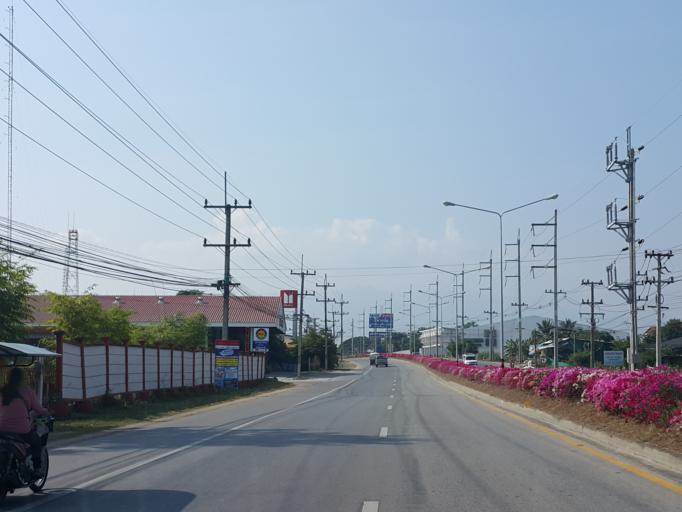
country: TH
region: Chiang Mai
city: Chom Thong
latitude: 18.4415
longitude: 98.6916
